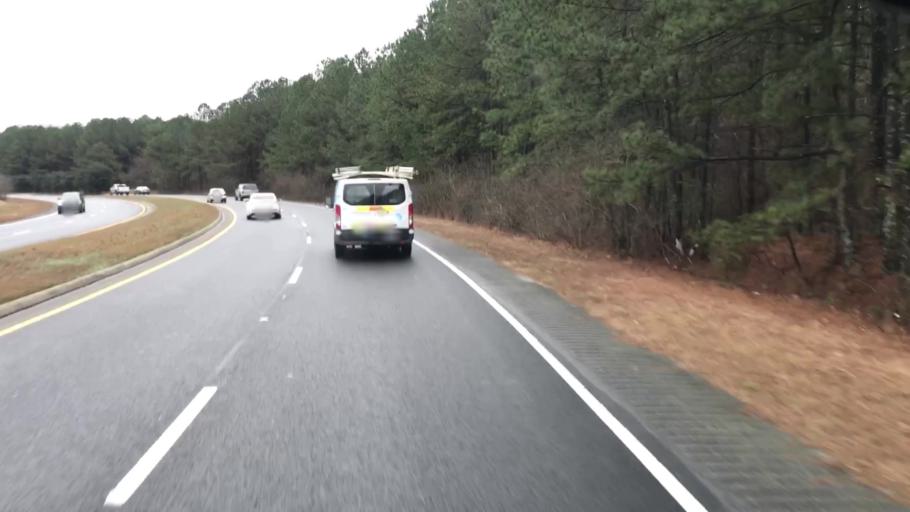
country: US
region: Georgia
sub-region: Gwinnett County
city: Snellville
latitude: 33.8759
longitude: -84.0239
